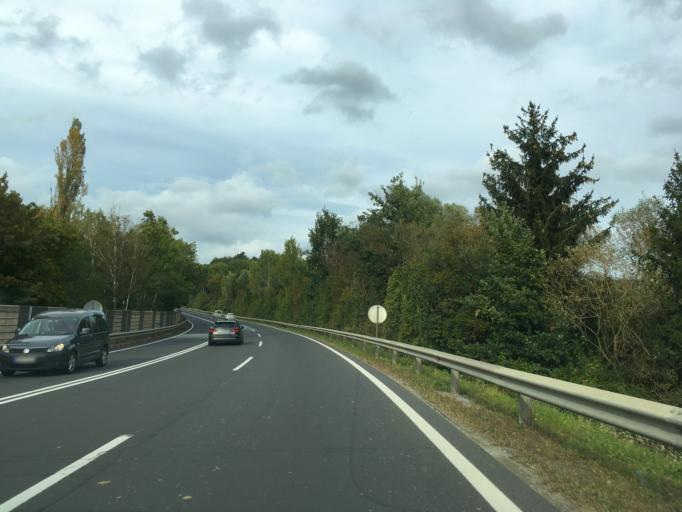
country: AT
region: Styria
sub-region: Politischer Bezirk Hartberg-Fuerstenfeld
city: Grafendorf bei Hartberg
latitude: 47.3376
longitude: 15.9954
